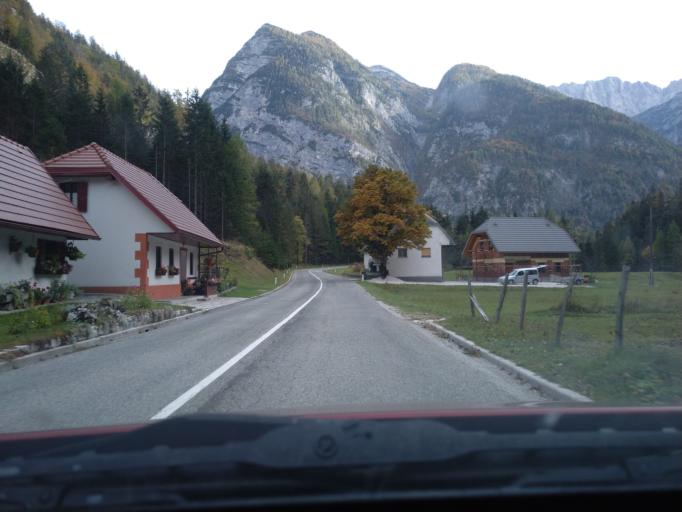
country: SI
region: Kranjska Gora
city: Kranjska Gora
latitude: 46.3884
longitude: 13.7488
